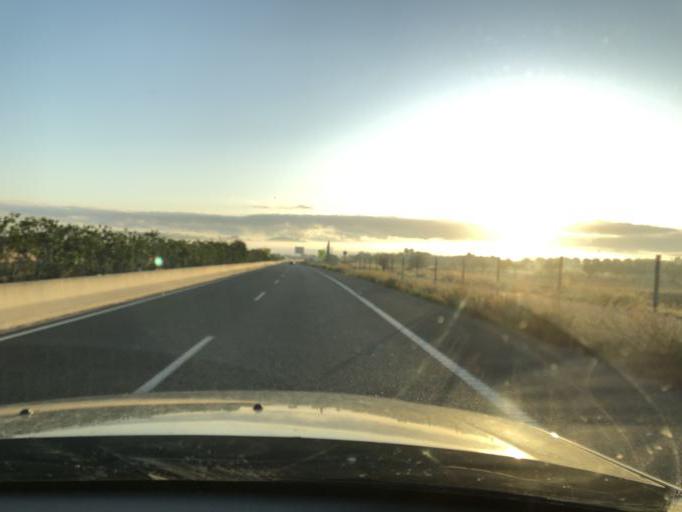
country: ES
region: Balearic Islands
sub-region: Illes Balears
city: Montuiri
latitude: 39.5620
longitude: 2.9637
